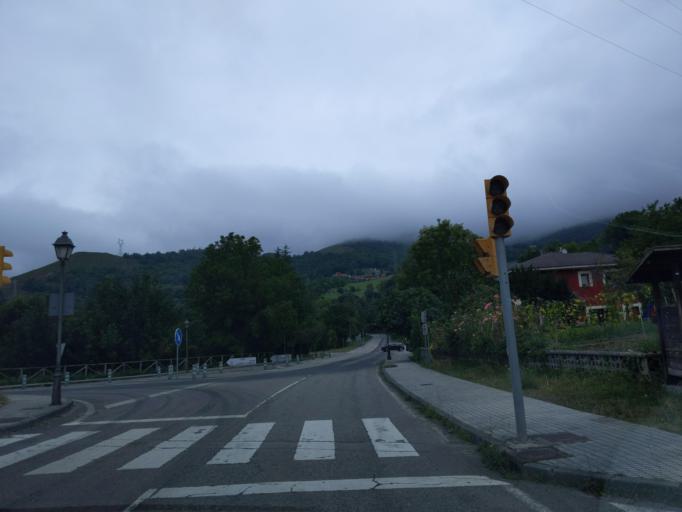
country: ES
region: Asturias
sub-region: Province of Asturias
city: Pola de Laviana
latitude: 43.2220
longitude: -5.4577
